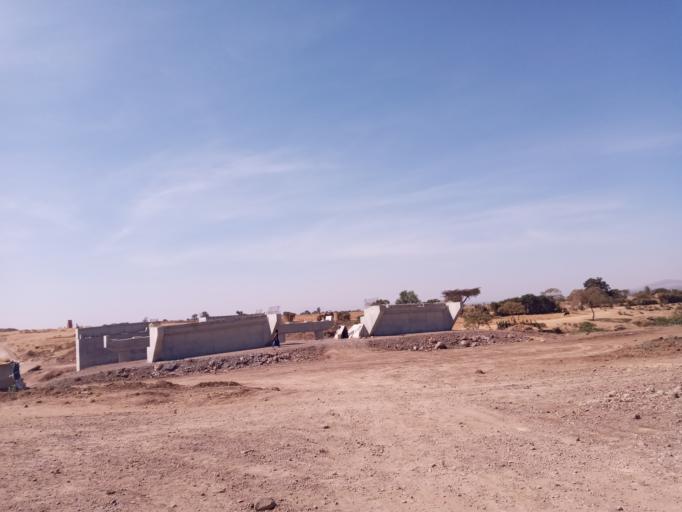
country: ET
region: Oromiya
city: Shashemene
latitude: 7.3672
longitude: 38.6448
